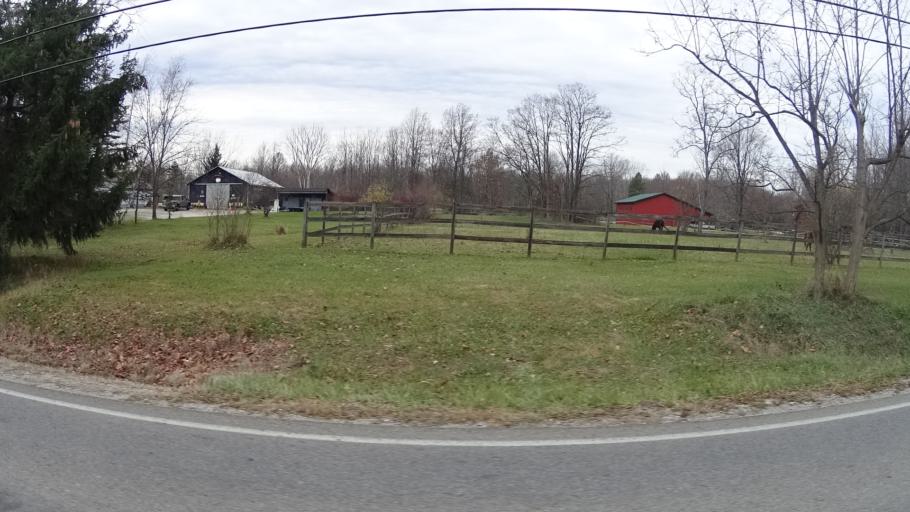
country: US
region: Ohio
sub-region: Cuyahoga County
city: Strongsville
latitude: 41.2920
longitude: -81.8779
